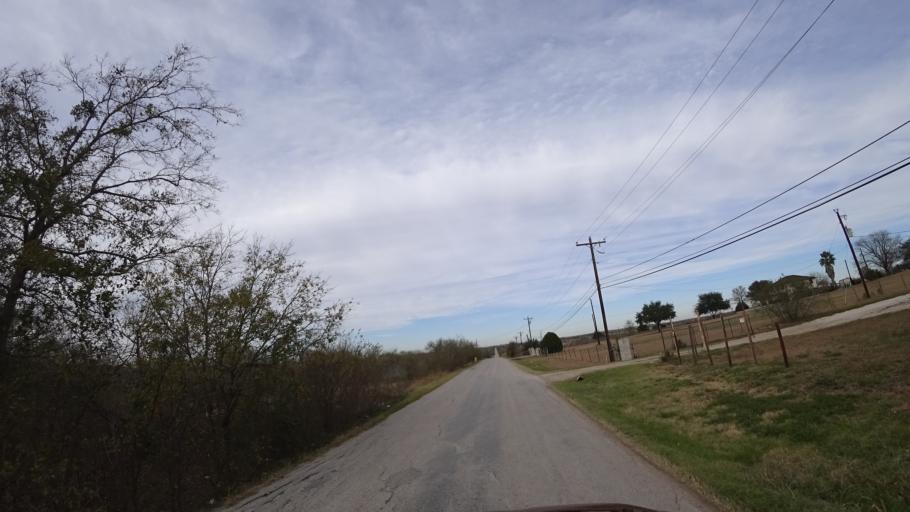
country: US
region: Texas
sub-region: Travis County
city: Garfield
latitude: 30.1119
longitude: -97.5848
